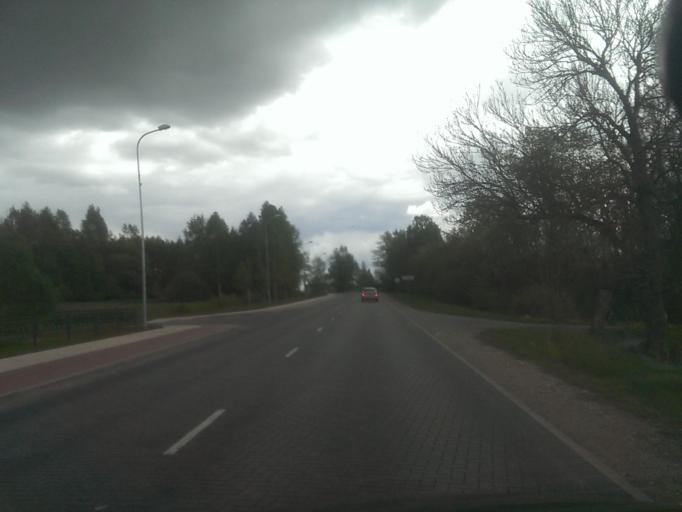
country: LV
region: Kuldigas Rajons
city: Kuldiga
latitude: 56.9822
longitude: 21.9377
